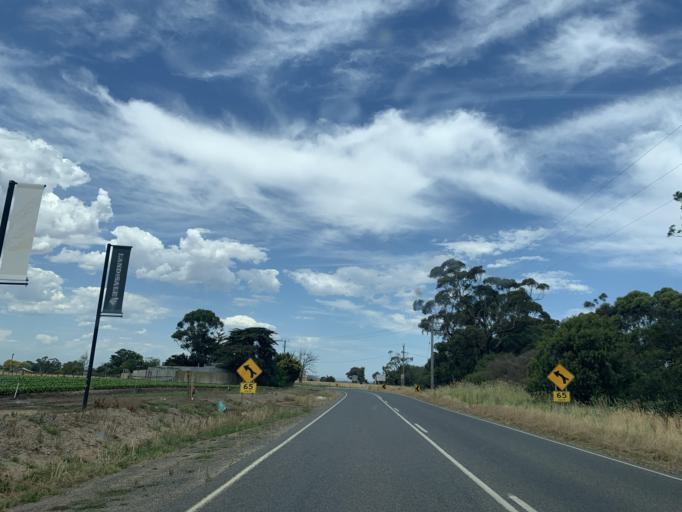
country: AU
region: Victoria
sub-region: Casey
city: Junction Village
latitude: -38.1338
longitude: 145.3334
